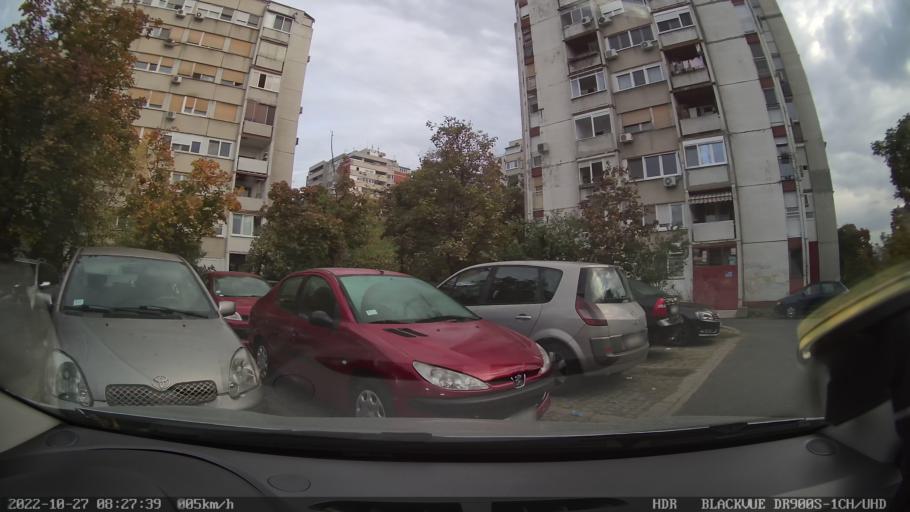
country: RS
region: Central Serbia
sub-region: Belgrade
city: Novi Beograd
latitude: 44.8010
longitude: 20.3963
